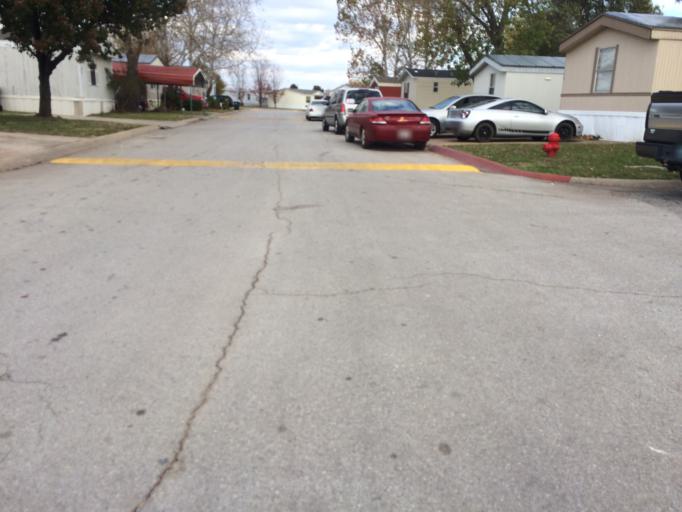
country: US
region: Oklahoma
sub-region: Cleveland County
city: Norman
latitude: 35.2404
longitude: -97.4523
